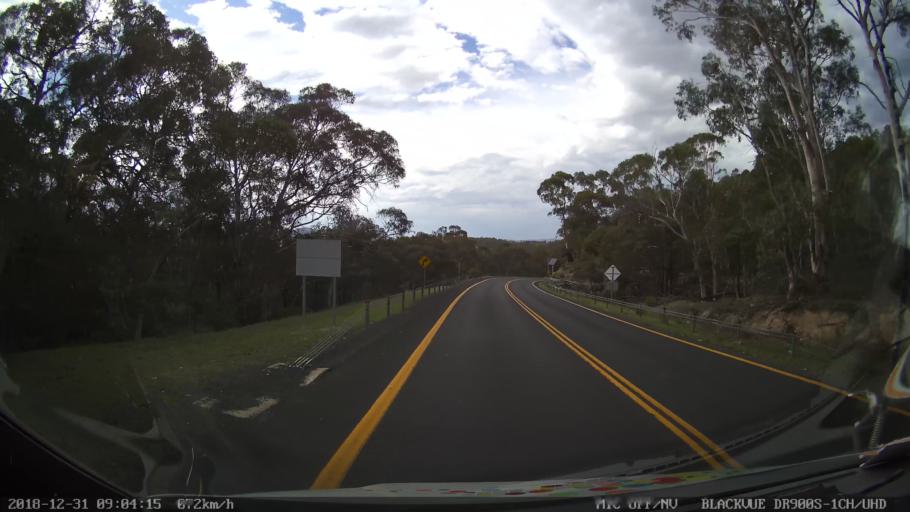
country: AU
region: New South Wales
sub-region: Snowy River
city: Jindabyne
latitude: -36.3522
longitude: 148.5860
